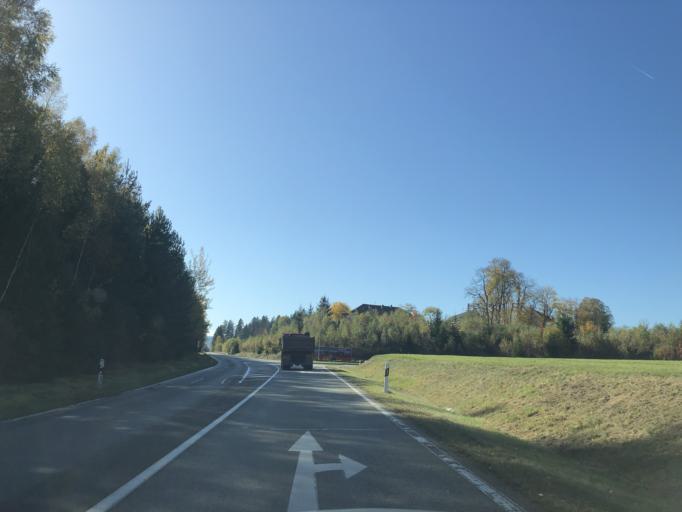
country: DE
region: Bavaria
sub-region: Lower Bavaria
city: Bobrach
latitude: 49.0516
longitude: 13.0332
